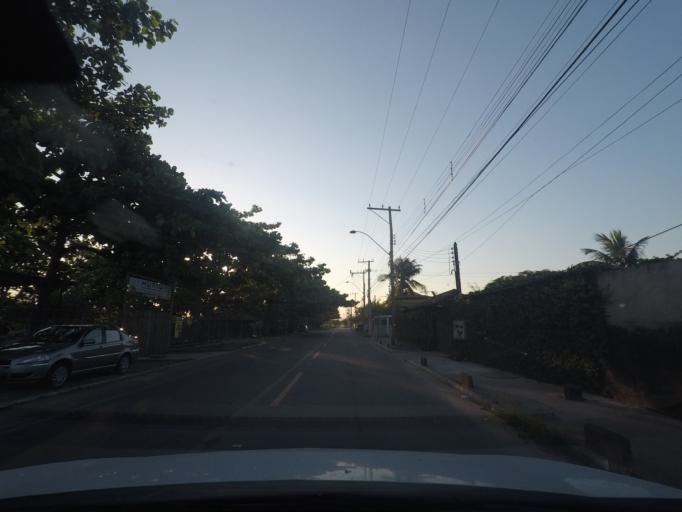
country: BR
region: Rio de Janeiro
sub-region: Marica
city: Marica
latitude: -22.9697
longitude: -42.9410
